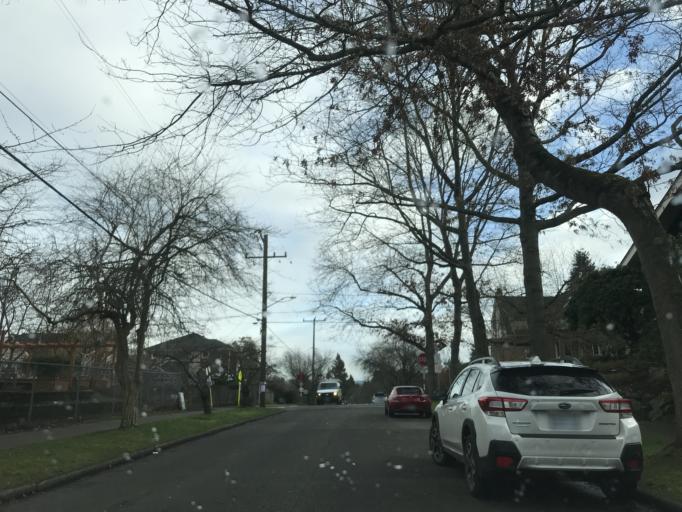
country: US
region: Washington
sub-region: King County
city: Seattle
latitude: 47.6403
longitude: -122.3045
